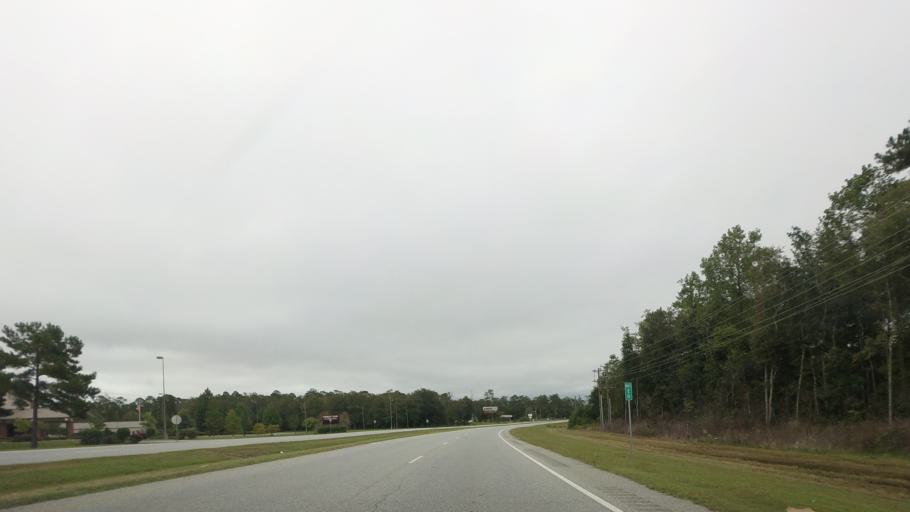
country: US
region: Georgia
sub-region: Lowndes County
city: Valdosta
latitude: 30.8806
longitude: -83.2445
